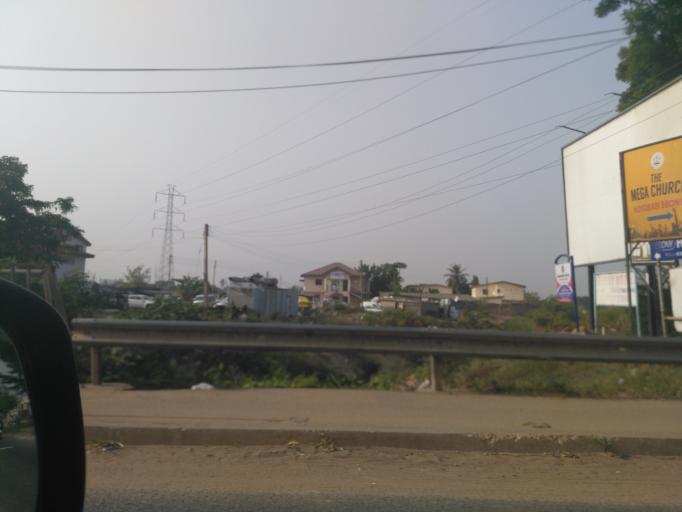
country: GH
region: Greater Accra
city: Accra
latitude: 5.6056
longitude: -0.2045
